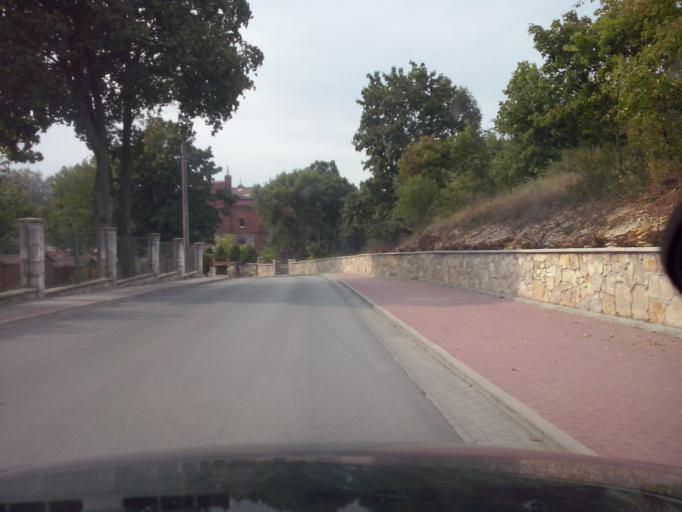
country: PL
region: Swietokrzyskie
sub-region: Powiat kielecki
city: Morawica
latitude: 50.7494
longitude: 20.6214
